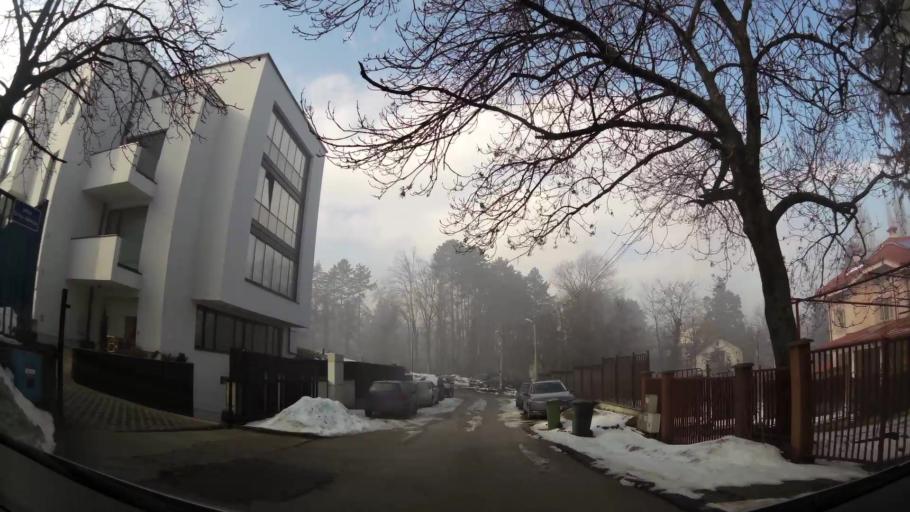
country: BG
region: Sofia-Capital
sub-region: Stolichna Obshtina
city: Sofia
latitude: 42.6510
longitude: 23.2604
